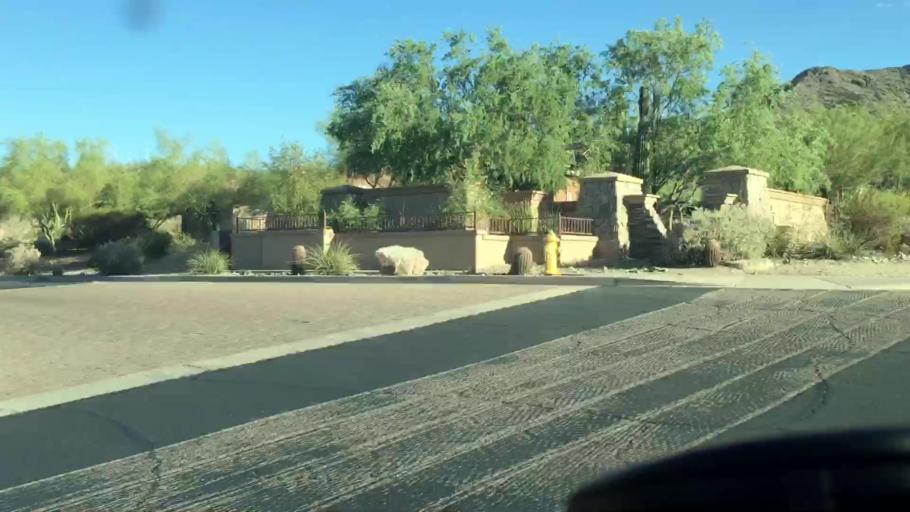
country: US
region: Arizona
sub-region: Maricopa County
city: Laveen
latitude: 33.3577
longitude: -112.0984
